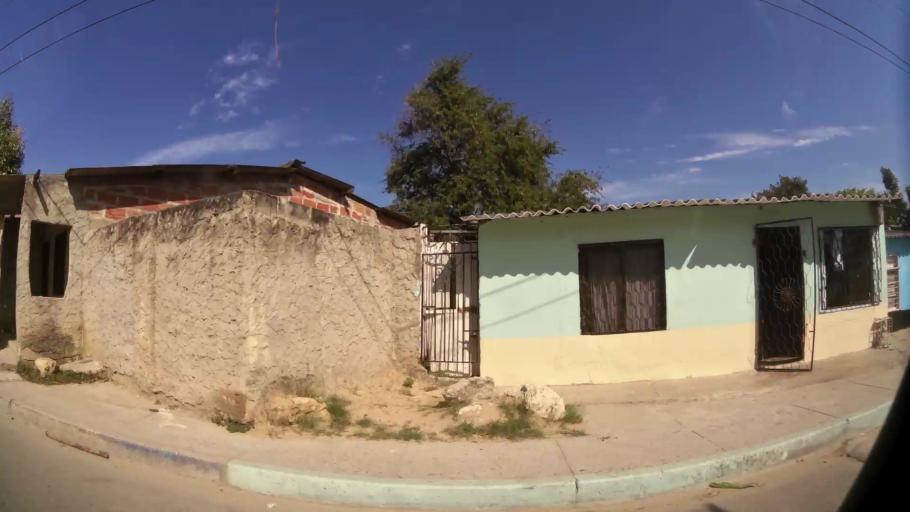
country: CO
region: Atlantico
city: Soledad
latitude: 10.9249
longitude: -74.8161
